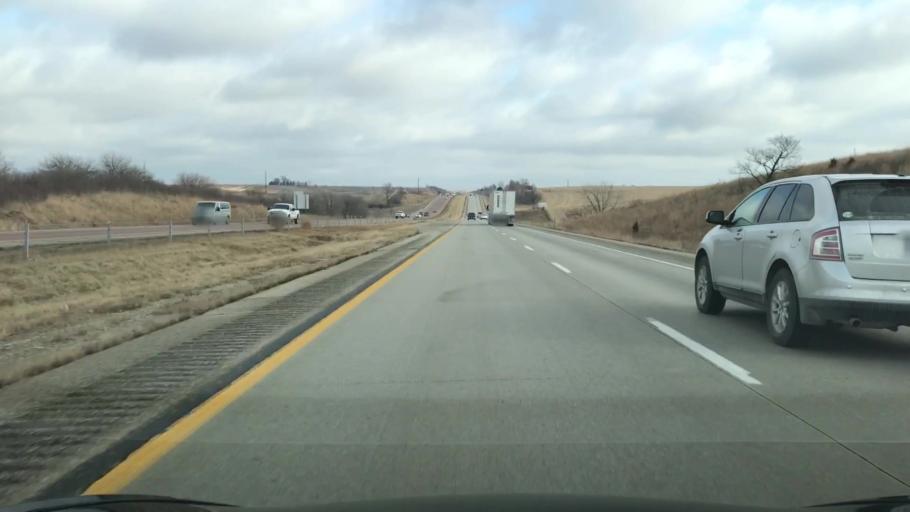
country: US
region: Iowa
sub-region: Guthrie County
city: Guthrie Center
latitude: 41.4930
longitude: -94.6210
